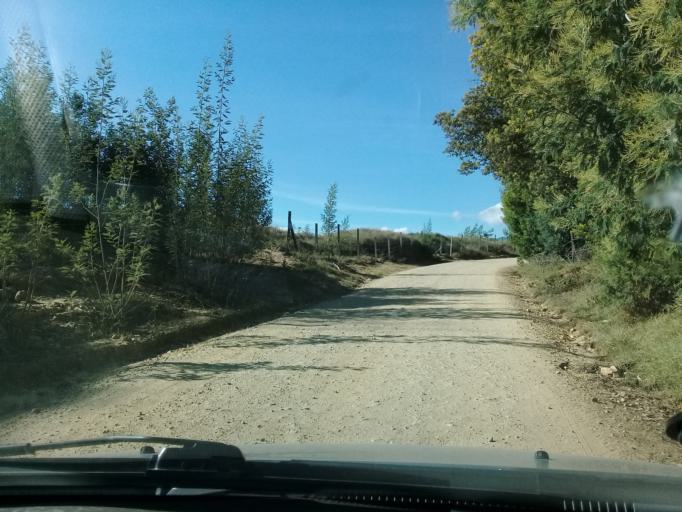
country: CO
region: Cundinamarca
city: Guatavita
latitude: 4.9324
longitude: -73.8792
